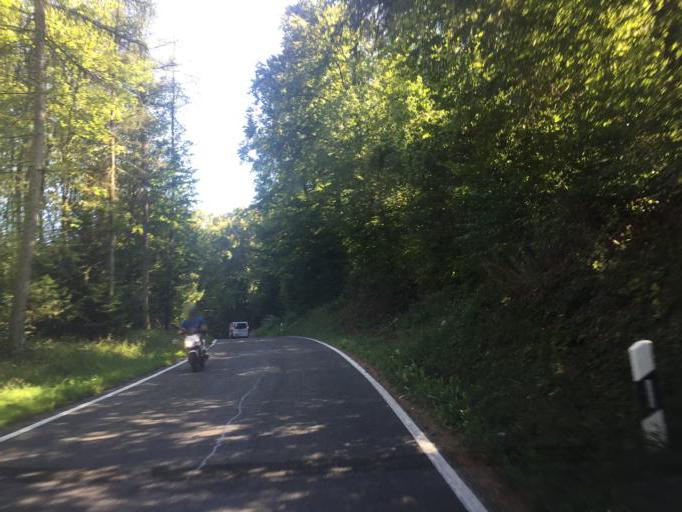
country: DE
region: Baden-Wuerttemberg
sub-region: Freiburg Region
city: Busingen
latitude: 47.7103
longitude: 8.6709
